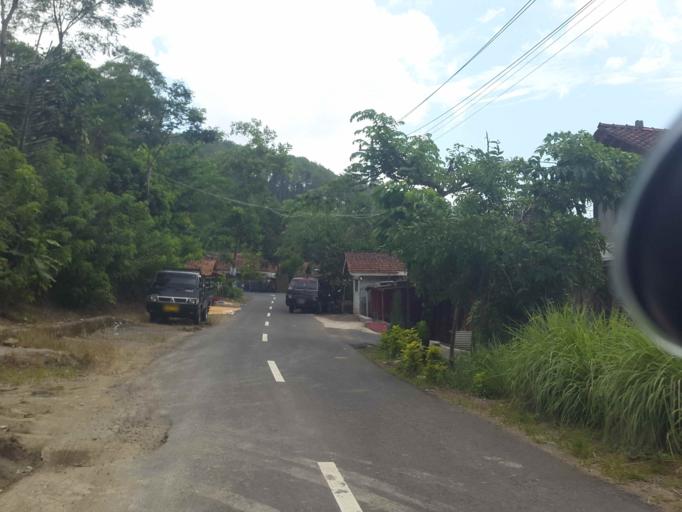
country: ID
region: Central Java
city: Pangawaren
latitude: -7.4284
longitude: 108.9506
